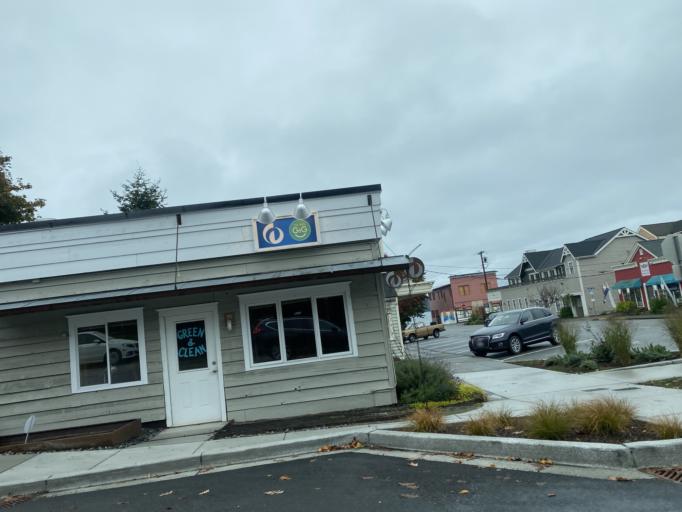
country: US
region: Washington
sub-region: Island County
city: Langley
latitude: 48.0400
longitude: -122.4096
